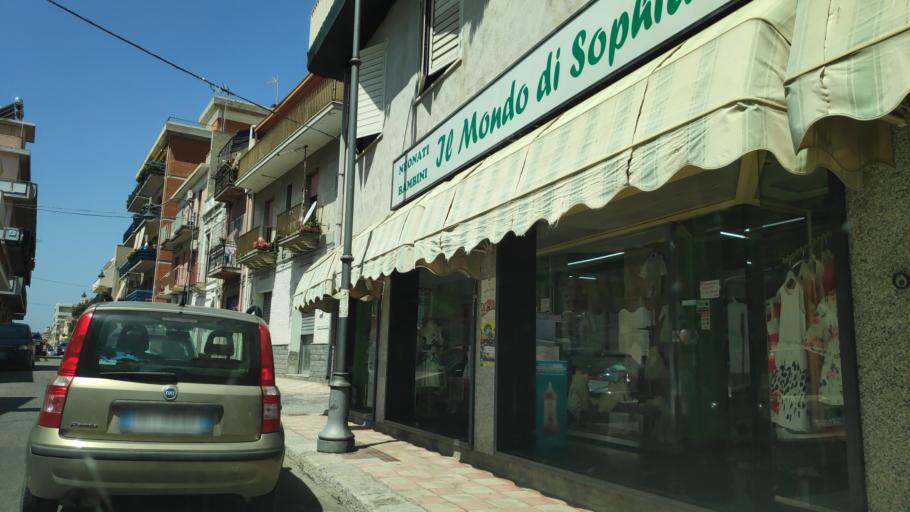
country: IT
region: Calabria
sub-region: Provincia di Reggio Calabria
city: Bova Marina
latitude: 37.9307
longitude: 15.9235
